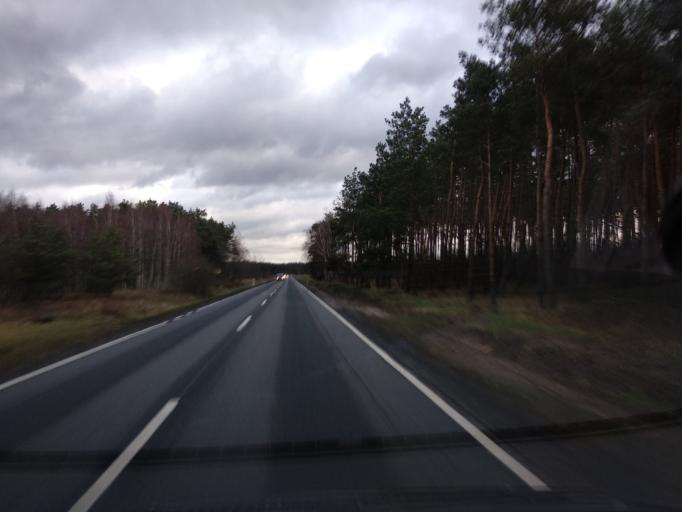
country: PL
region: Lower Silesian Voivodeship
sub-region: Powiat olesnicki
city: Miedzyborz
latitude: 51.4241
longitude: 17.6821
